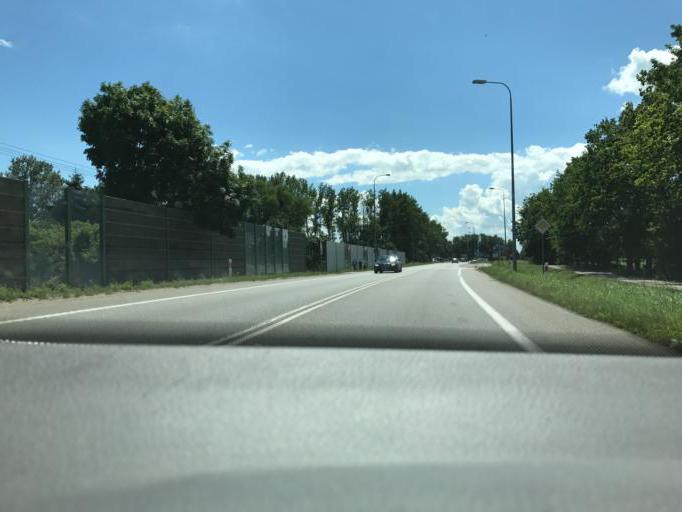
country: PL
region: Pomeranian Voivodeship
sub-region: Gdansk
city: Gdansk
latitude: 54.3311
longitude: 18.7444
